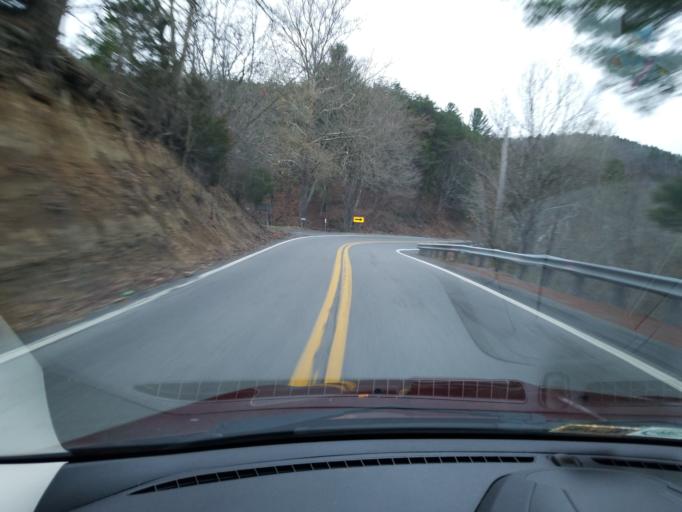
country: US
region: West Virginia
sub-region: Monroe County
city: Union
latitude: 37.5048
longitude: -80.6116
